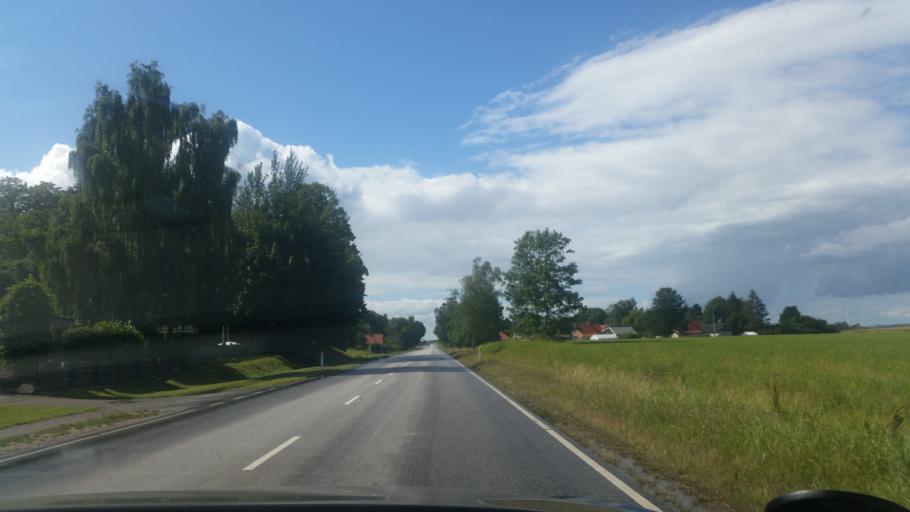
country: DK
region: Zealand
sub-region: Holbaek Kommune
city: Svinninge
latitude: 55.7353
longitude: 11.5505
